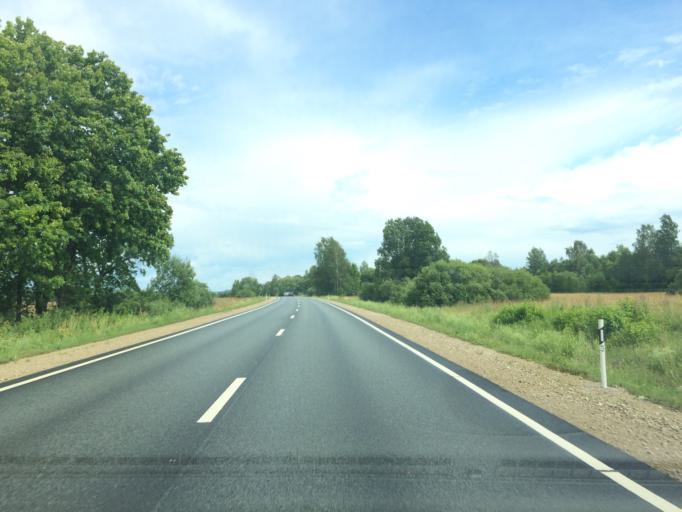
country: LV
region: Rezekne
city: Rezekne
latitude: 56.5317
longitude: 27.1860
